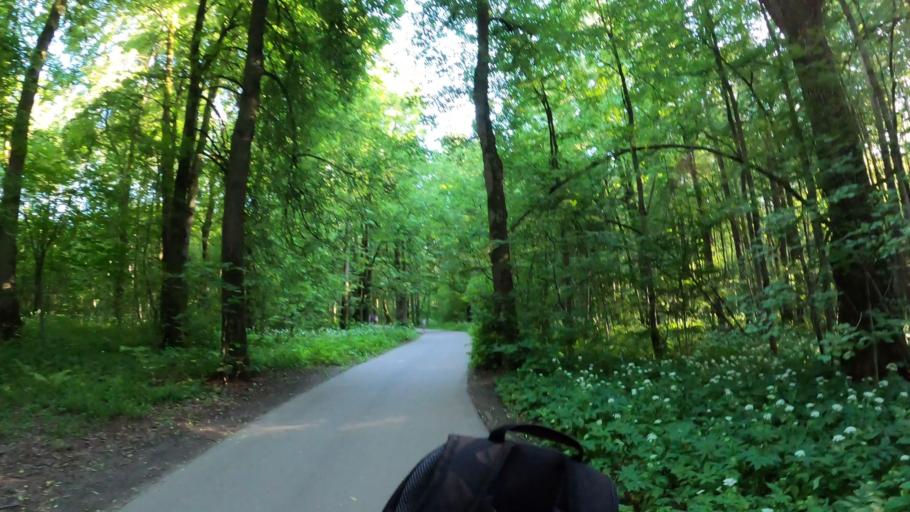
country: RU
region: Moscow
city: Zyuzino
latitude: 55.6183
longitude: 37.5594
